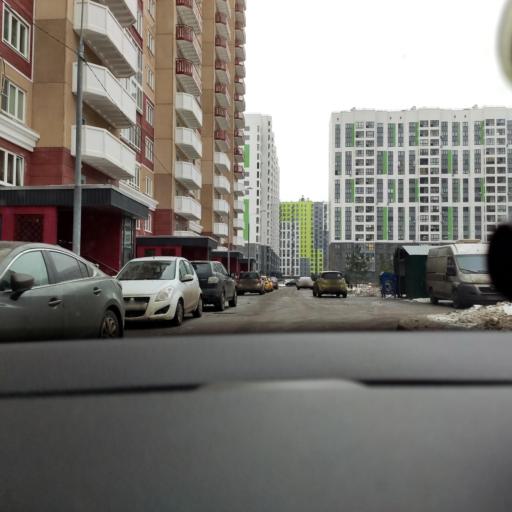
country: RU
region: Moskovskaya
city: Shcherbinka
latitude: 55.5237
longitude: 37.5917
